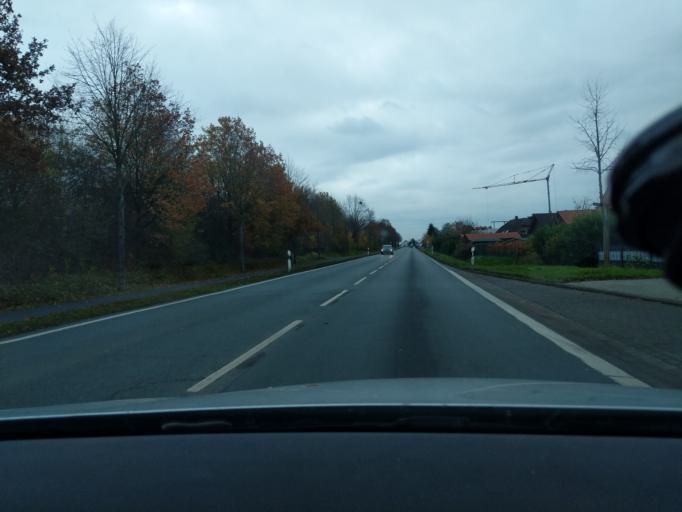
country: DE
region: North Rhine-Westphalia
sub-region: Regierungsbezirk Munster
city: Birgte
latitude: 52.2655
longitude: 7.6163
